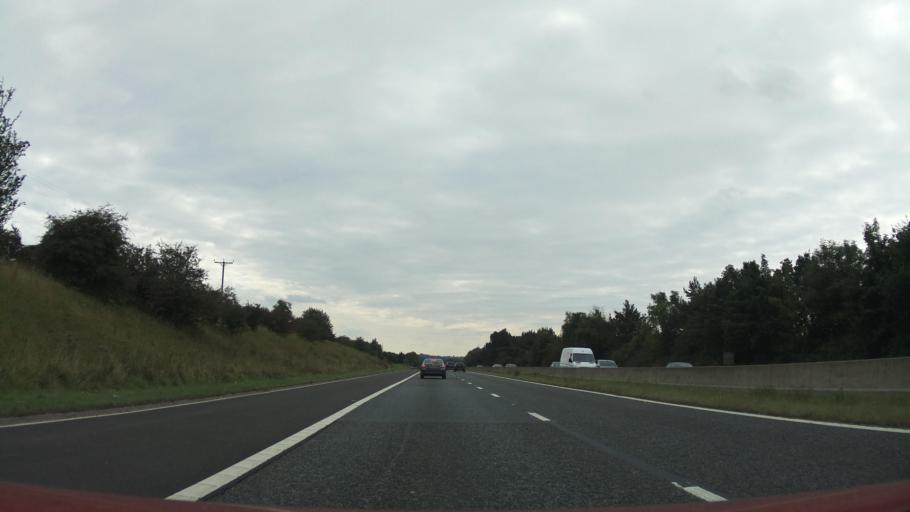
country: GB
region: England
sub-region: County Durham
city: West Rainton
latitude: 54.8323
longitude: -1.5237
